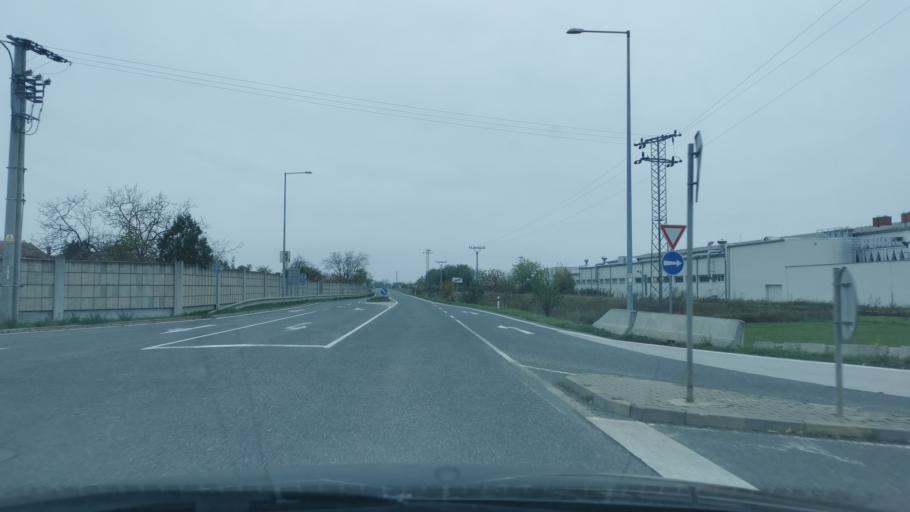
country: SK
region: Trnavsky
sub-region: Okres Skalica
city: Skalica
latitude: 48.8474
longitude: 17.2159
